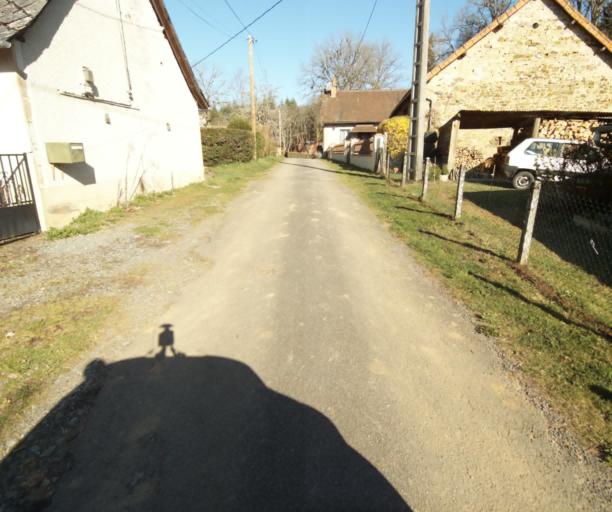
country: FR
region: Limousin
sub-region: Departement de la Correze
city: Seilhac
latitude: 45.3942
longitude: 1.7618
